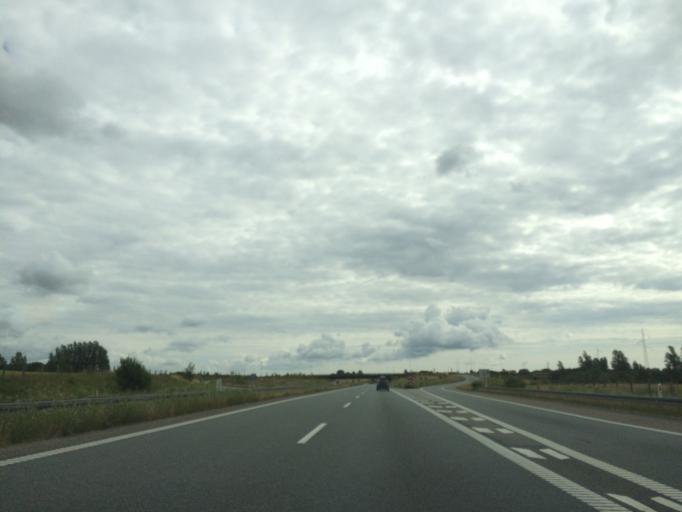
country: DK
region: Central Jutland
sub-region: Arhus Kommune
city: Lystrup
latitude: 56.2230
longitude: 10.2273
